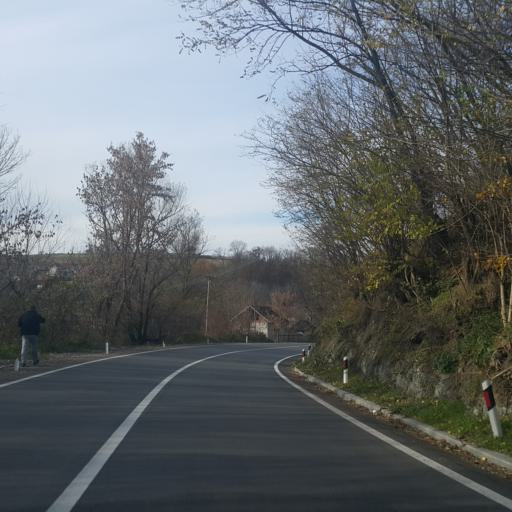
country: RS
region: Central Serbia
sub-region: Belgrade
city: Lazarevac
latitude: 44.3475
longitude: 20.4010
